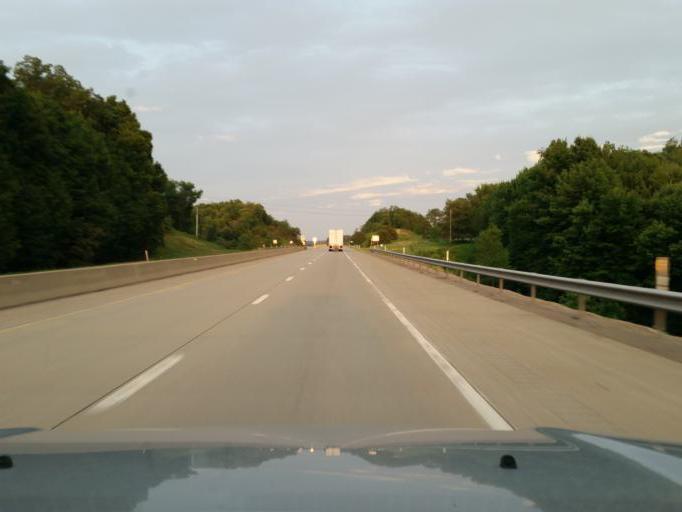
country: US
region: Pennsylvania
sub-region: Cambria County
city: Westmont
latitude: 40.4495
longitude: -78.9883
